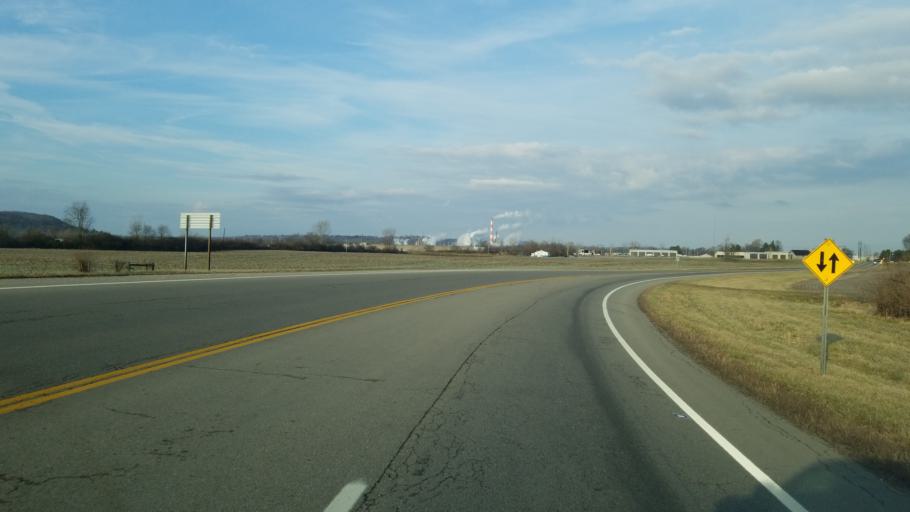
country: US
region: Ohio
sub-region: Ross County
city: Chillicothe
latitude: 39.3149
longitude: -82.9419
